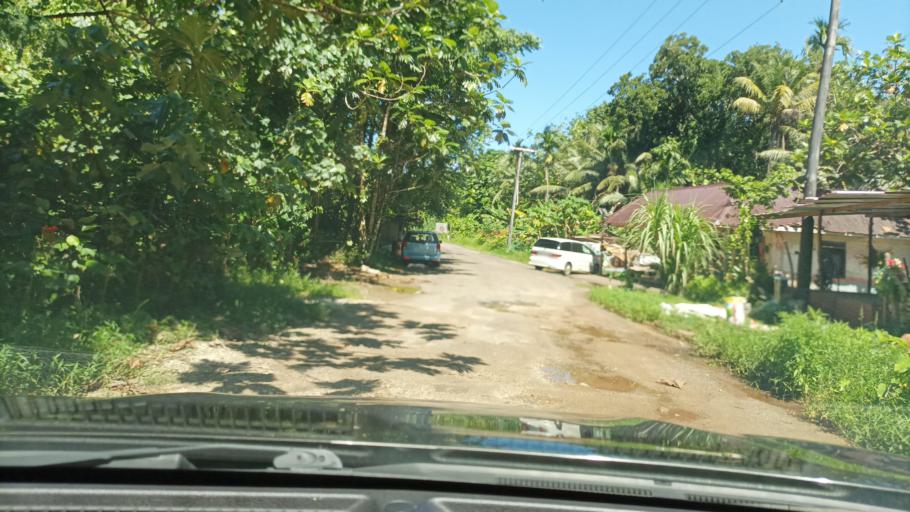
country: FM
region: Pohnpei
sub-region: Madolenihm Municipality
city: Madolenihm Municipality Government
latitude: 6.8431
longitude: 158.3059
